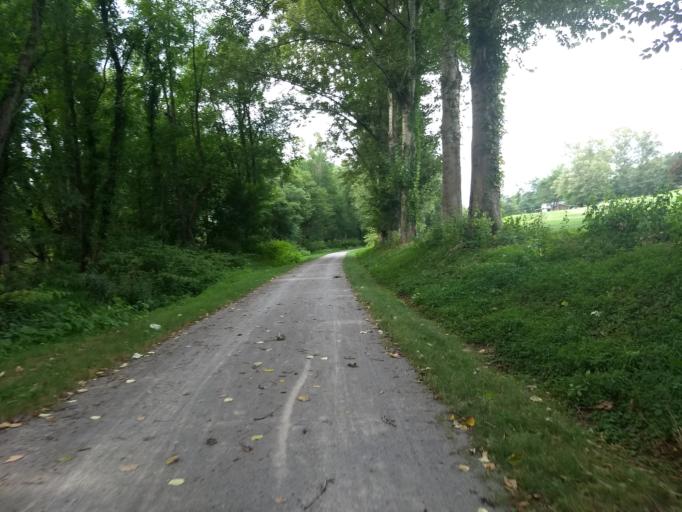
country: US
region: Pennsylvania
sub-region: Armstrong County
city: Freeport
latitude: 40.6629
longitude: -79.6925
